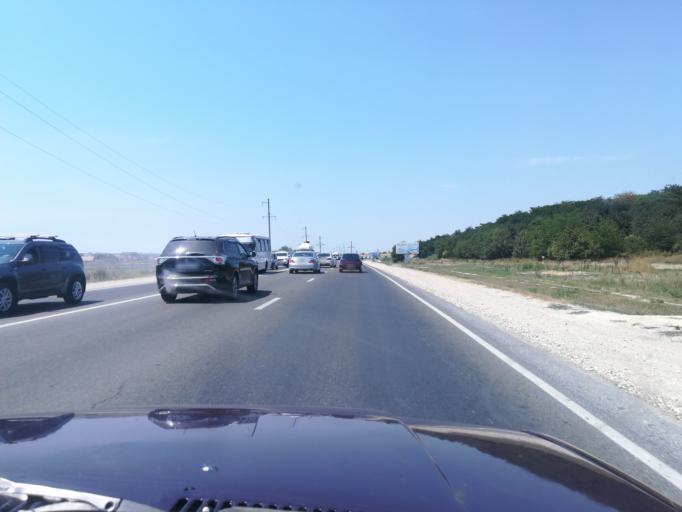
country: RU
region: Krasnodarskiy
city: Tsibanobalka
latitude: 44.9557
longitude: 37.3095
